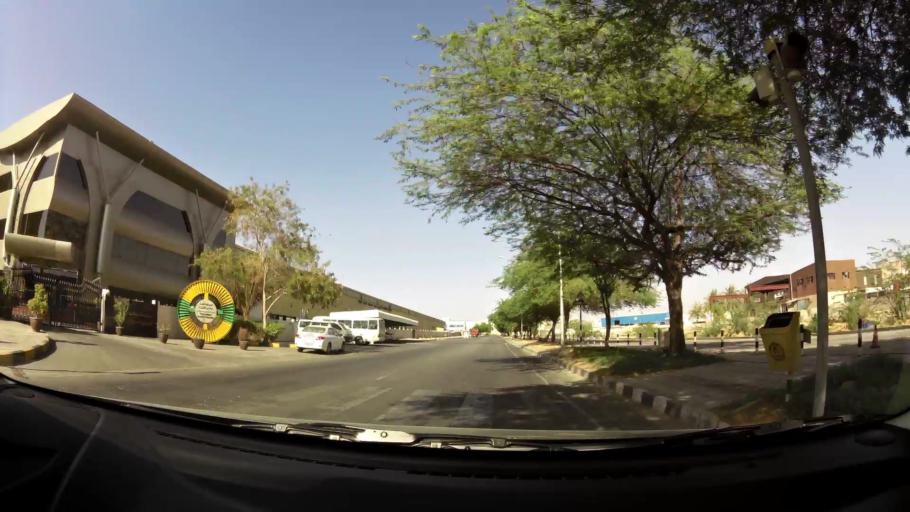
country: OM
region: Muhafazat Masqat
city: As Sib al Jadidah
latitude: 23.5575
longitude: 58.2090
